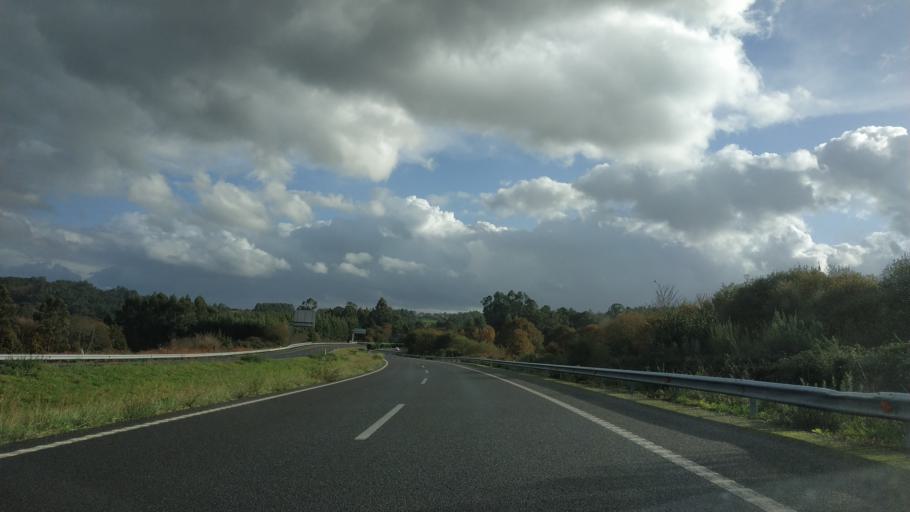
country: ES
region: Galicia
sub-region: Provincia da Coruna
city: Cambre
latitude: 43.2701
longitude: -8.3594
